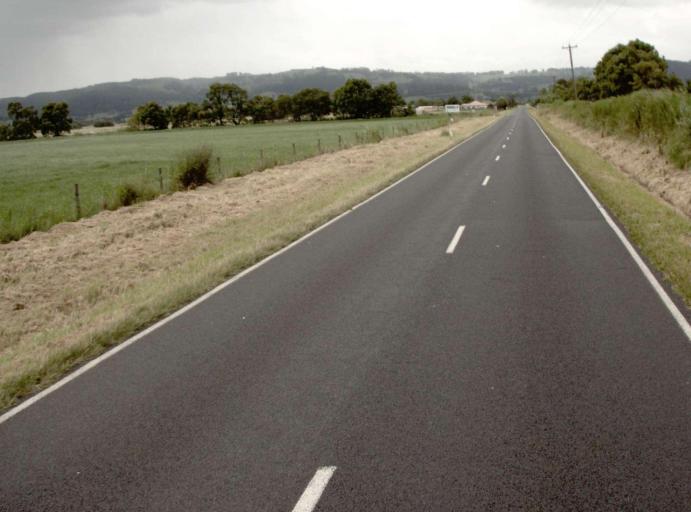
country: AU
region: Victoria
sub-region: Latrobe
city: Moe
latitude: -38.1753
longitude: 146.1455
